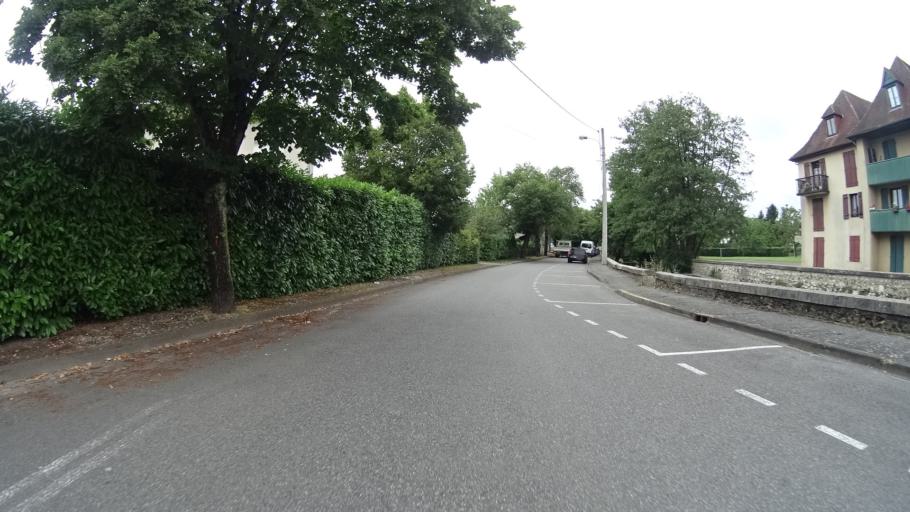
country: FR
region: Aquitaine
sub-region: Departement des Pyrenees-Atlantiques
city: Orthez
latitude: 43.4918
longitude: -0.7750
